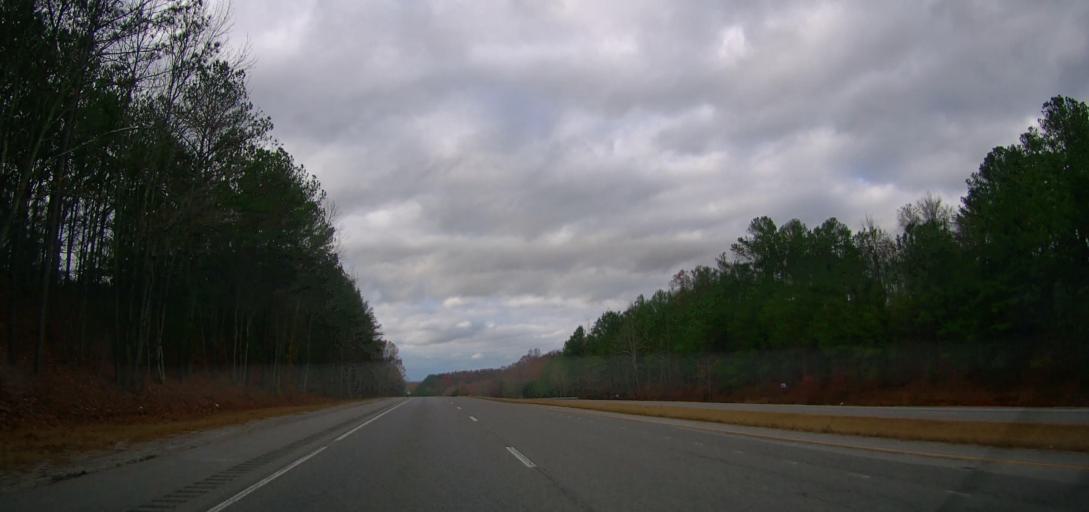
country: US
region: Alabama
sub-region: Lawrence County
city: Town Creek
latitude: 34.6211
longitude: -87.4692
